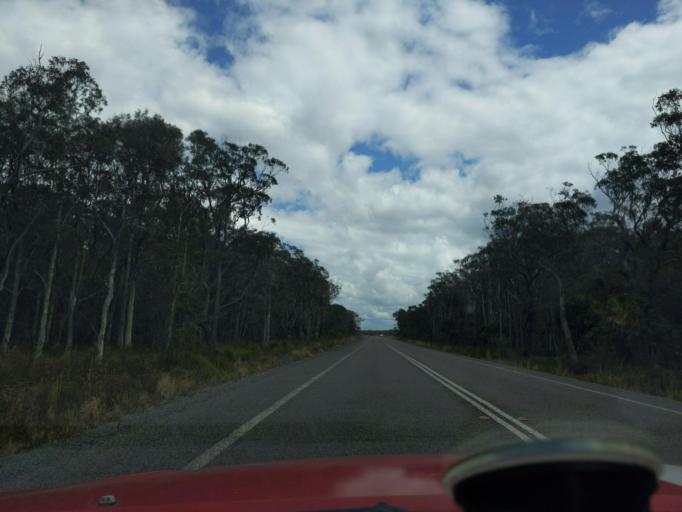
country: AU
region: New South Wales
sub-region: Great Lakes
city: Hawks Nest
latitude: -32.5916
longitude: 152.2639
